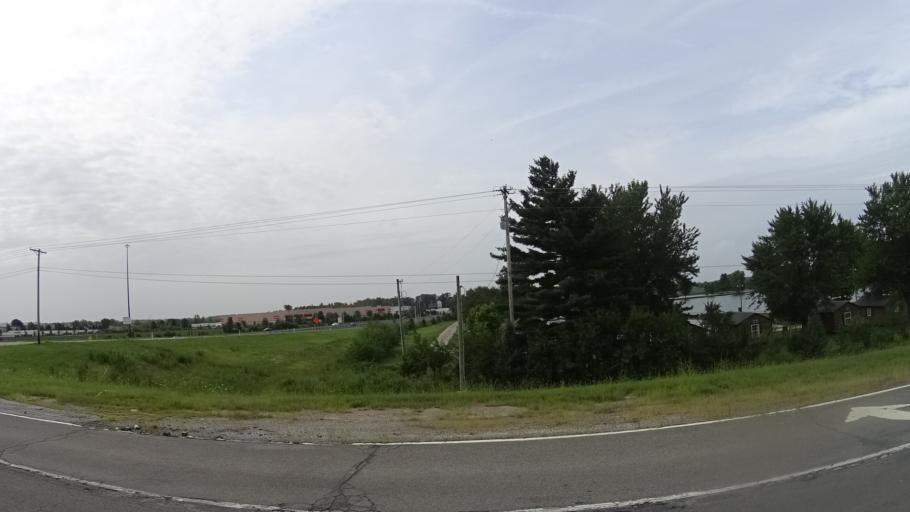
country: US
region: Indiana
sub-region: Madison County
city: Pendleton
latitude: 40.0051
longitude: -85.7745
